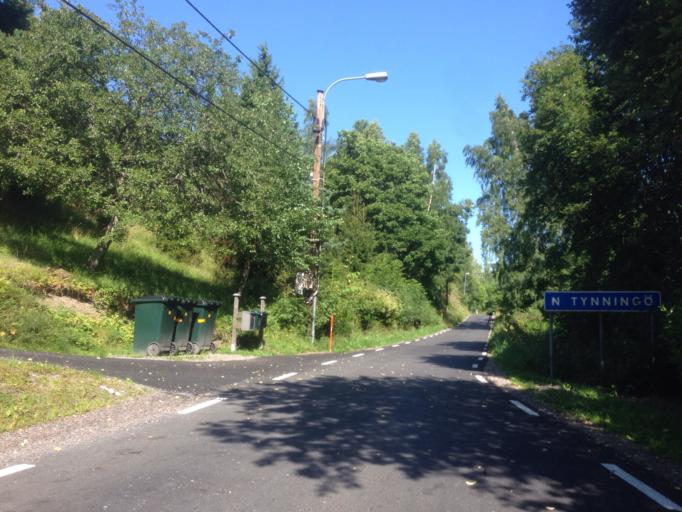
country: SE
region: Stockholm
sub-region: Vaxholms Kommun
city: Vaxholm
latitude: 59.3898
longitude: 18.3751
